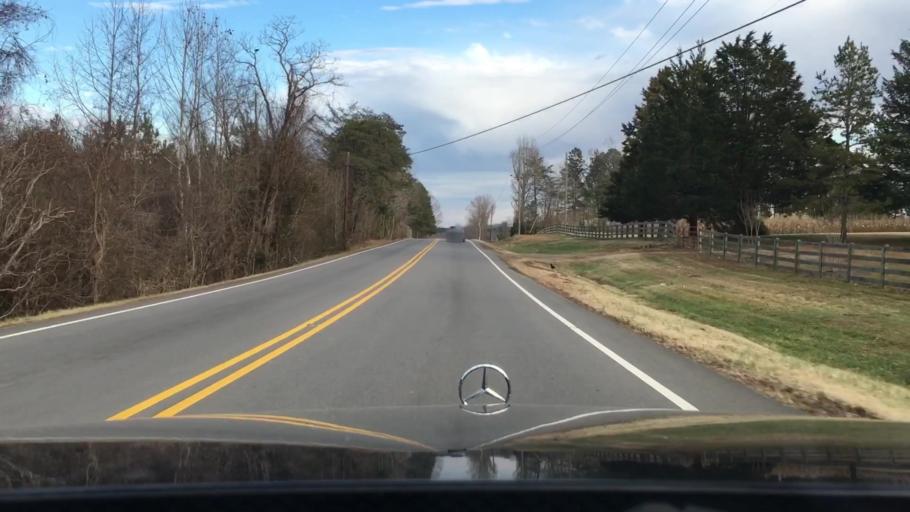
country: US
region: North Carolina
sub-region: Caswell County
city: Yanceyville
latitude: 36.4067
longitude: -79.3140
